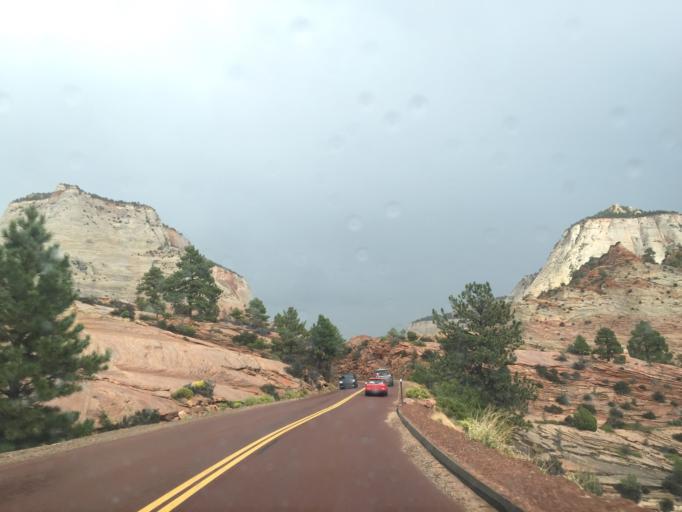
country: US
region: Utah
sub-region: Washington County
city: Hildale
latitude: 37.2231
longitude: -112.9054
